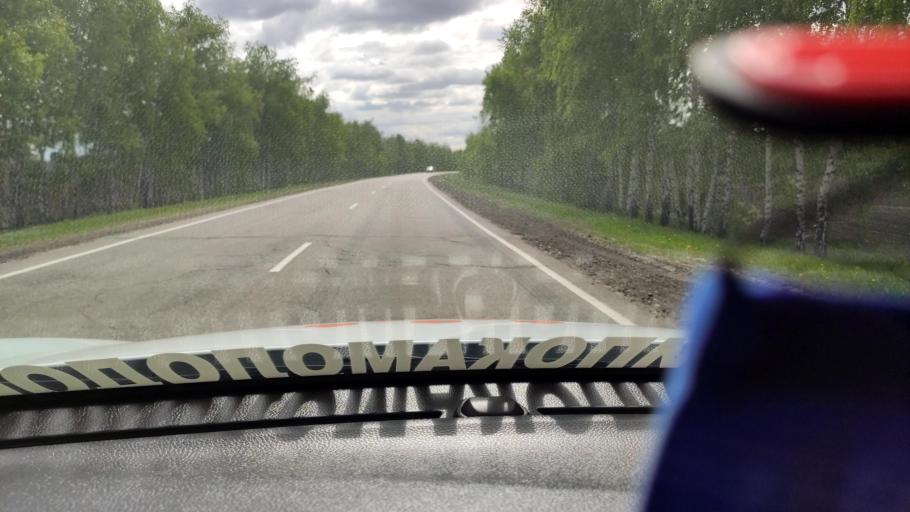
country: RU
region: Voronezj
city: Liski
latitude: 50.7964
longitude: 39.3640
